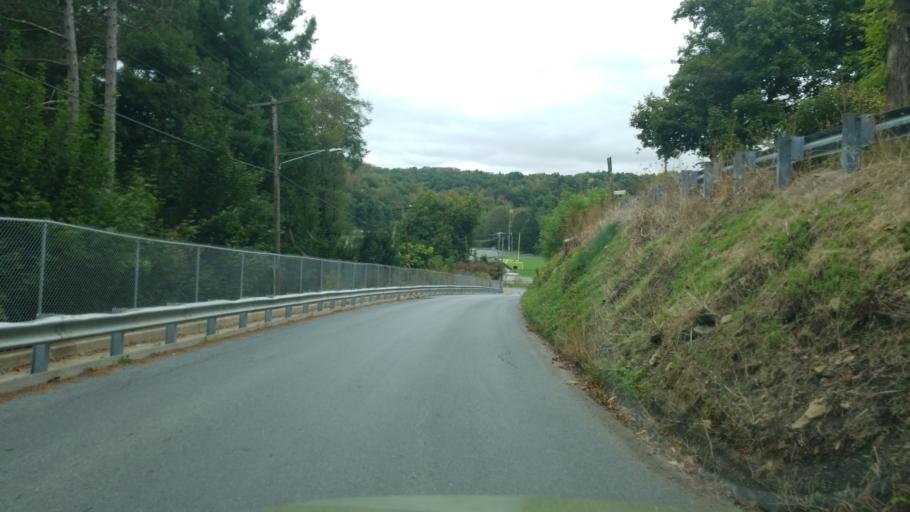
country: US
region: Pennsylvania
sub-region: Clearfield County
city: Curwensville
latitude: 40.9727
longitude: -78.5184
